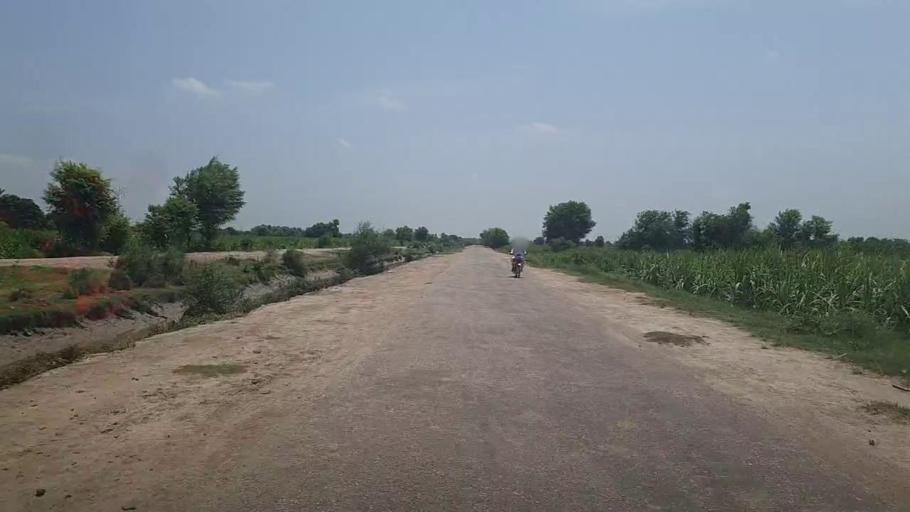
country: PK
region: Sindh
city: Ubauro
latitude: 28.2952
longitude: 69.8041
